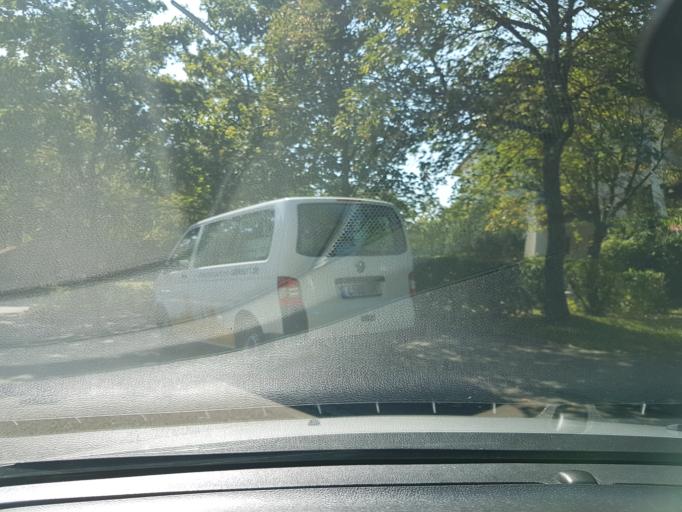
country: DE
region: Bavaria
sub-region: Upper Bavaria
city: Unterschleissheim
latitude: 48.2733
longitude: 11.5760
